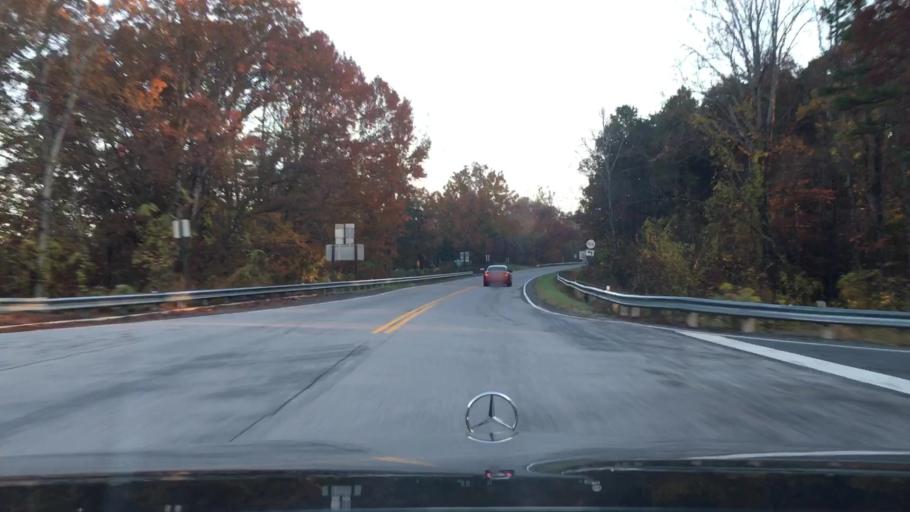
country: US
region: Virginia
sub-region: Campbell County
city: Altavista
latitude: 37.1290
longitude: -79.3072
